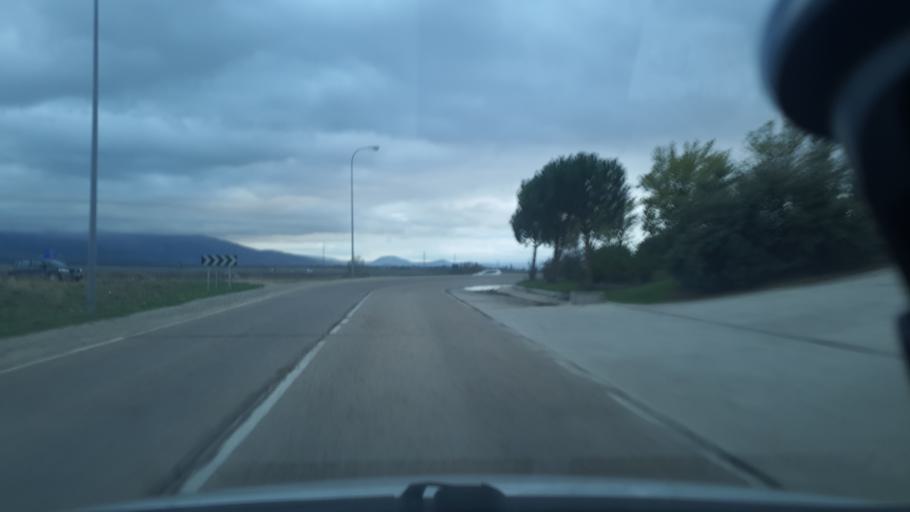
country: ES
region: Castille and Leon
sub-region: Provincia de Segovia
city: San Cristobal de Segovia
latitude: 40.9270
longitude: -4.0920
